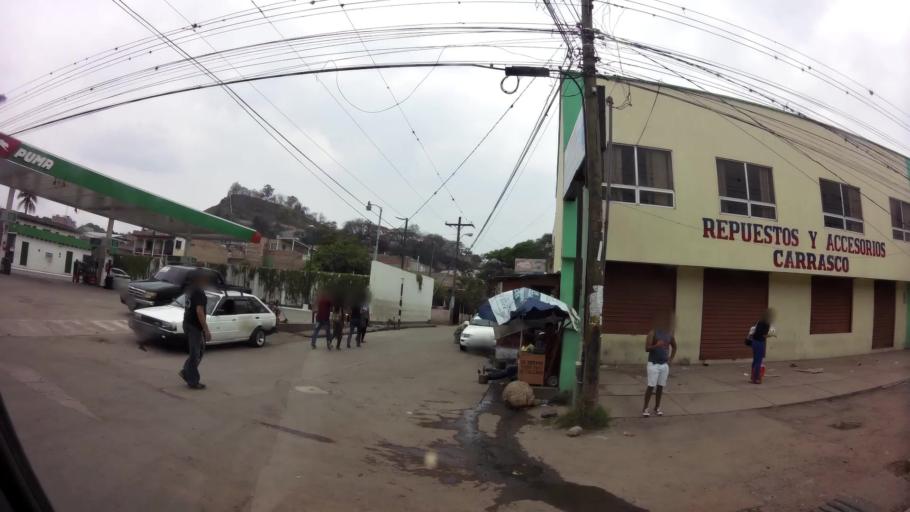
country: HN
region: Francisco Morazan
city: Tegucigalpa
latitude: 14.0666
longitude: -87.2113
